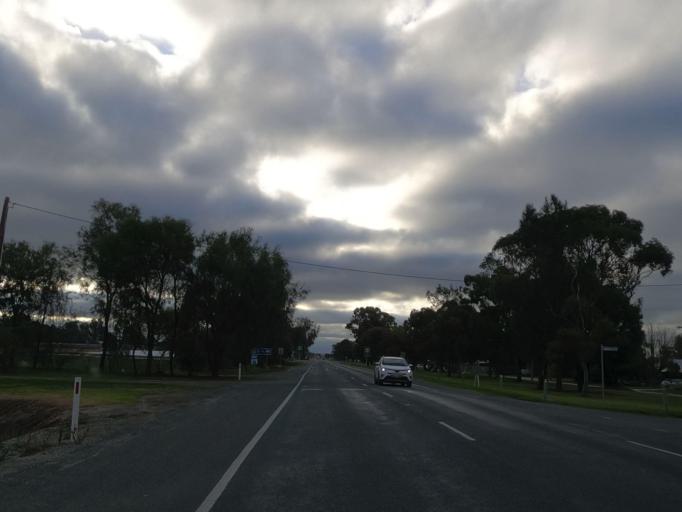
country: AU
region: Victoria
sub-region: Swan Hill
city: Swan Hill
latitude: -35.7428
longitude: 143.9208
